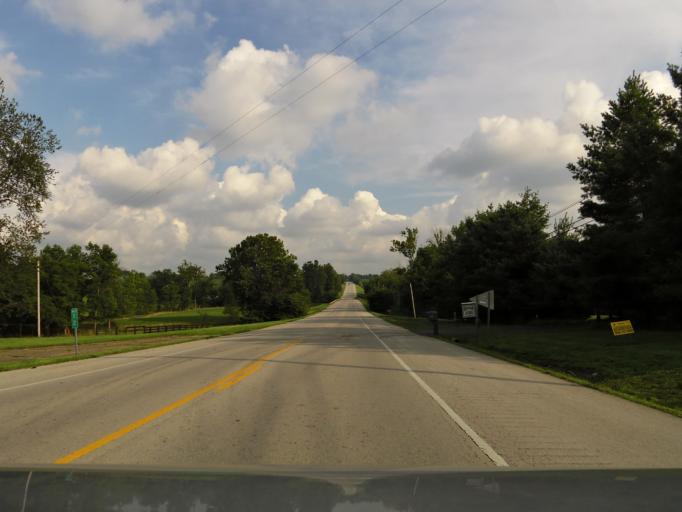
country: US
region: Kentucky
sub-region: Bourbon County
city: Paris
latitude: 38.2663
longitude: -84.2963
